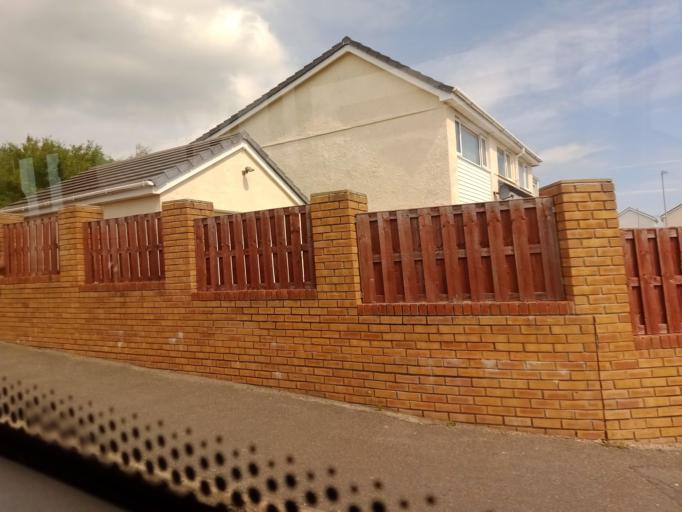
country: GB
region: Wales
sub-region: Gwynedd
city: Bangor
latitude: 53.2429
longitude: -4.1455
